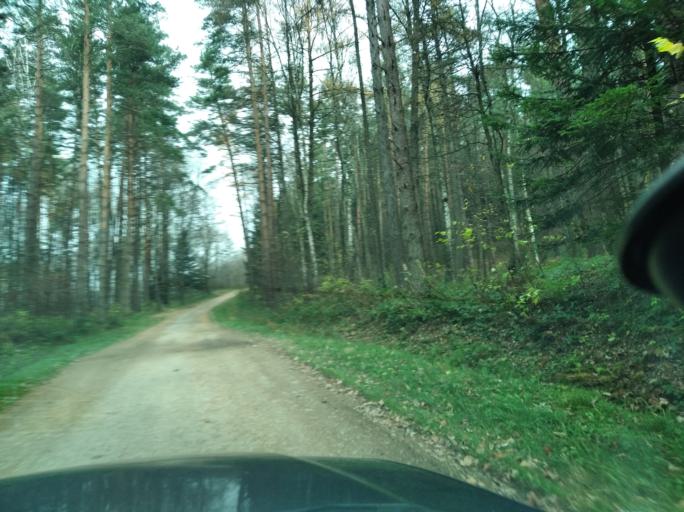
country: PL
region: Subcarpathian Voivodeship
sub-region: Powiat strzyzowski
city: Wysoka Strzyzowska
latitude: 49.7926
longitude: 21.7684
